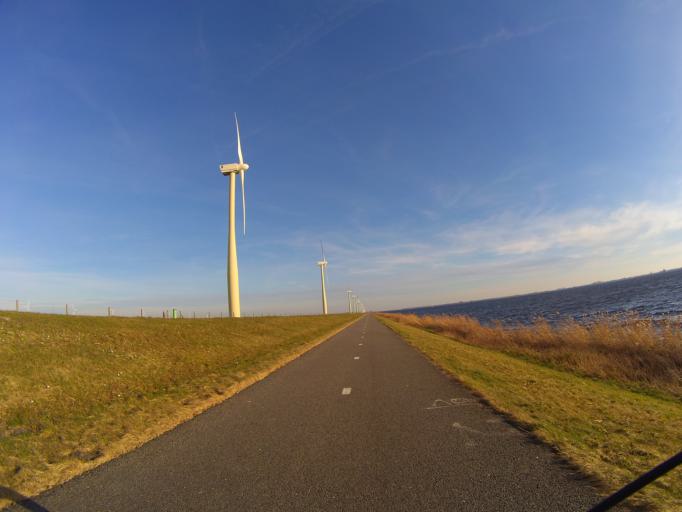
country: NL
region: Utrecht
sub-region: Gemeente Bunschoten
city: Spakenburg
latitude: 52.2936
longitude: 5.3354
